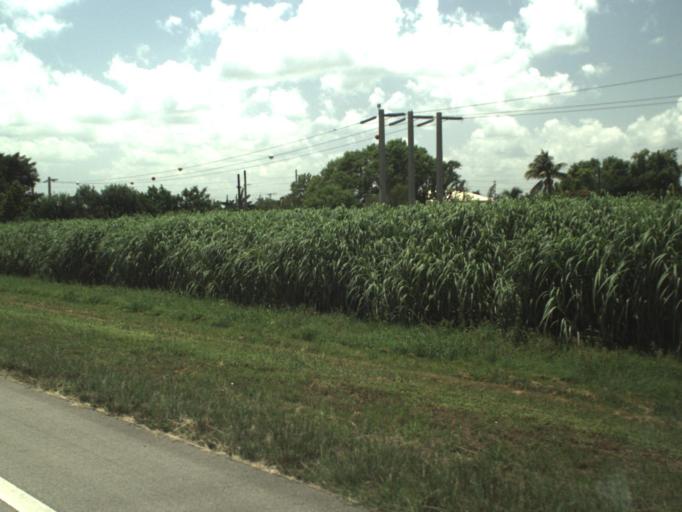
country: US
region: Florida
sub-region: Palm Beach County
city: Belle Glade
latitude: 26.6994
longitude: -80.6681
